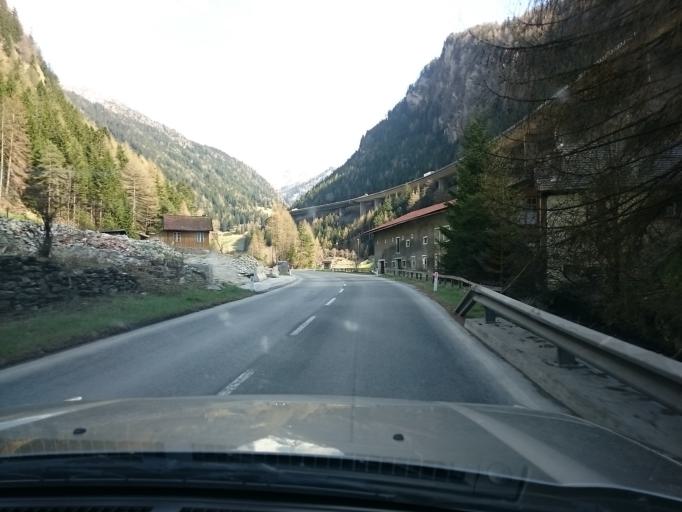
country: AT
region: Tyrol
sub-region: Politischer Bezirk Innsbruck Land
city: Gries am Brenner
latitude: 47.0298
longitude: 11.4897
